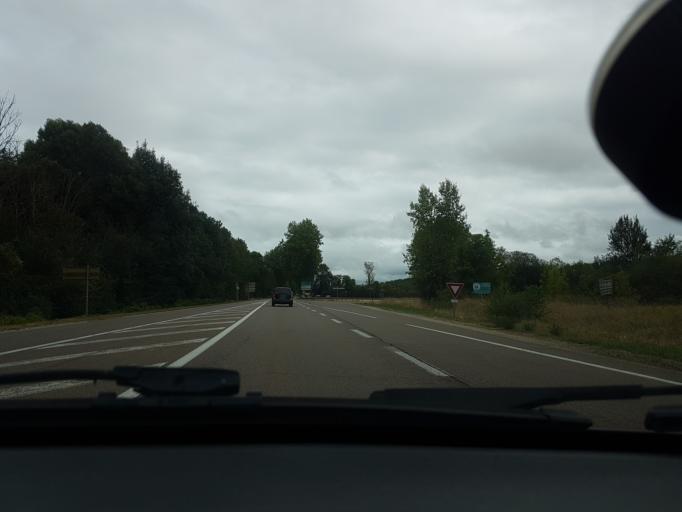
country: FR
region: Bourgogne
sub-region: Departement de l'Yonne
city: Champs-sur-Yonne
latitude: 47.7238
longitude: 3.6074
